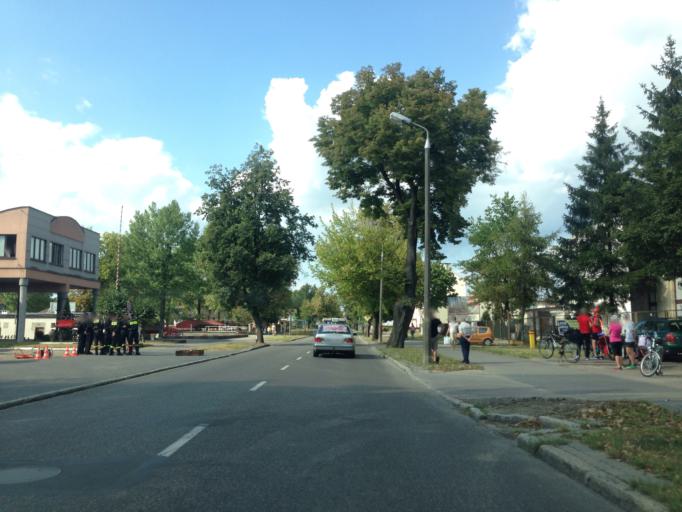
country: PL
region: Warmian-Masurian Voivodeship
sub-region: Powiat ilawski
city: Ilawa
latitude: 53.5889
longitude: 19.5709
